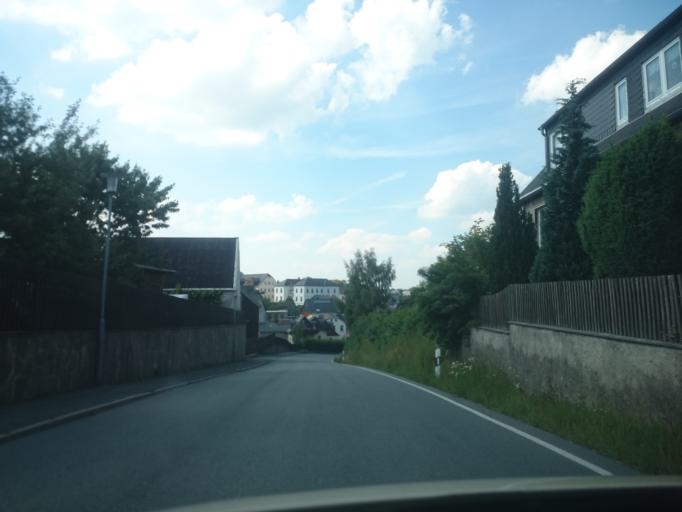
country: DE
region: Saxony
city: Lengefeld
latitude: 50.7165
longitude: 13.1962
